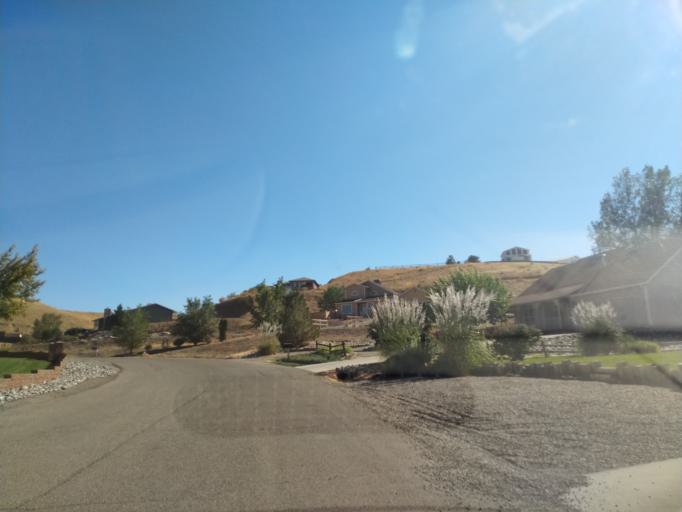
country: US
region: Colorado
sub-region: Mesa County
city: Orchard Mesa
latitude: 39.0248
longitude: -108.5158
